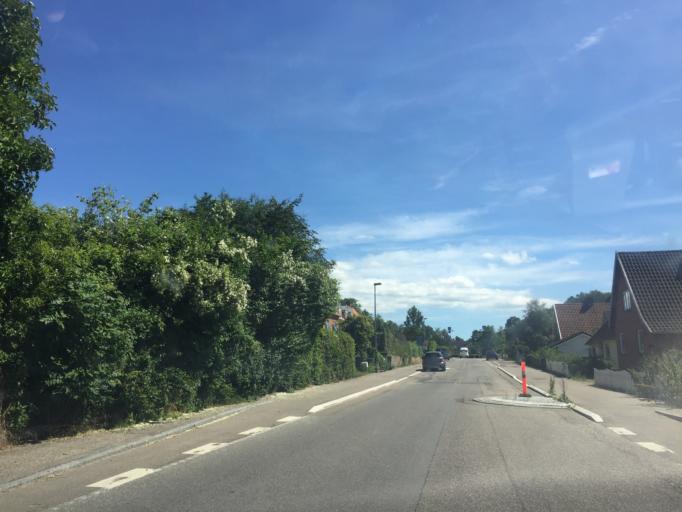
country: DK
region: Capital Region
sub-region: Halsnaes Kommune
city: Frederiksvaerk
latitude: 55.9543
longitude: 12.0245
